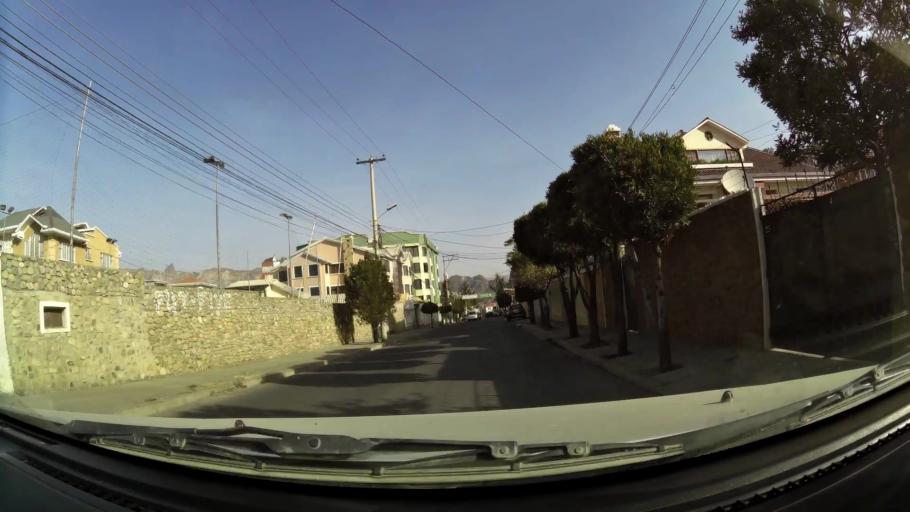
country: BO
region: La Paz
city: La Paz
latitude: -16.5252
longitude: -68.0880
